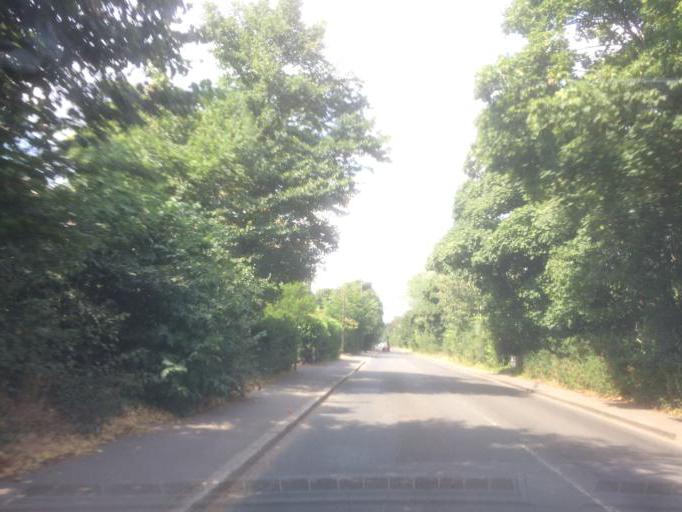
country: GB
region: England
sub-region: Buckinghamshire
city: Farnham Royal
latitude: 51.5401
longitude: -0.6166
